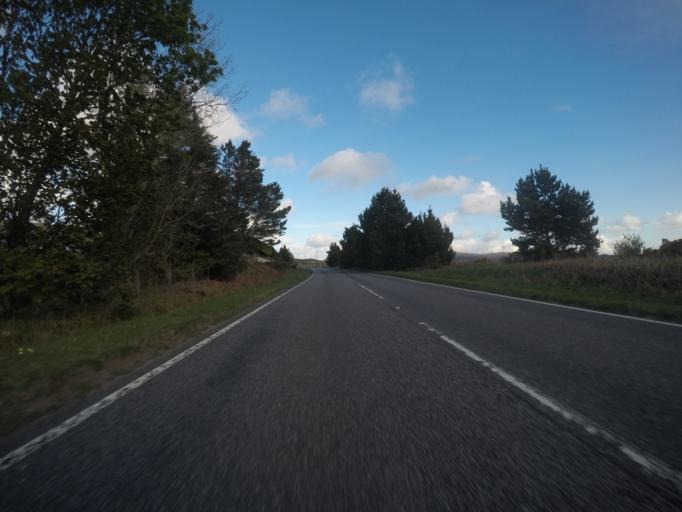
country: GB
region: Scotland
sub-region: Highland
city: Portree
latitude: 57.4525
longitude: -6.2662
